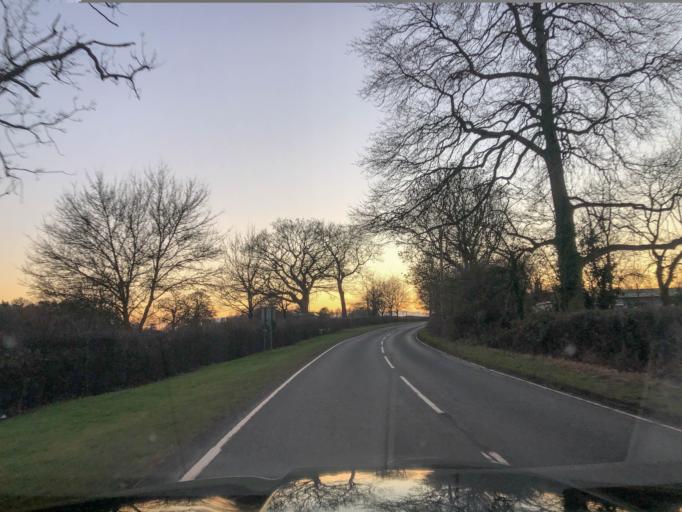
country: GB
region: England
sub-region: Warwickshire
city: Kenilworth
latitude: 52.3255
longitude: -1.5864
